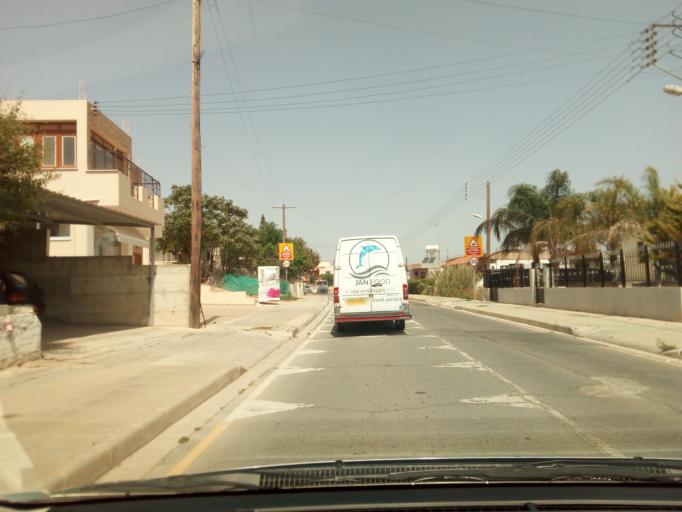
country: CY
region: Larnaka
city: Xylotymbou
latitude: 34.9887
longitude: 33.7808
